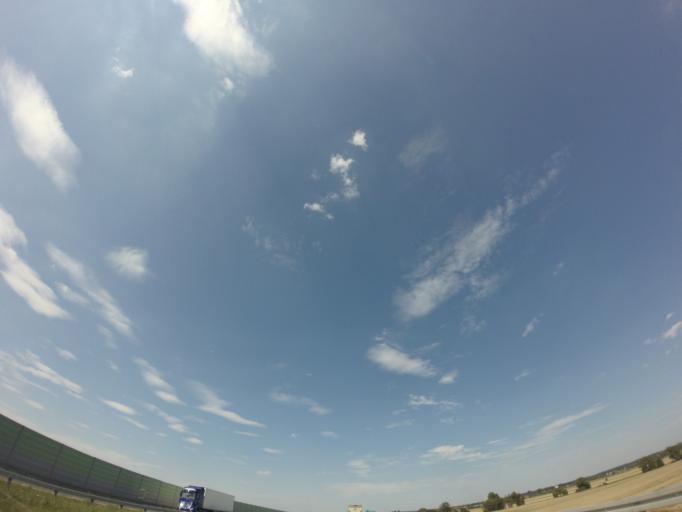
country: PL
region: Lower Silesian Voivodeship
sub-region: Legnica
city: Legnica
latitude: 51.2361
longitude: 16.1432
